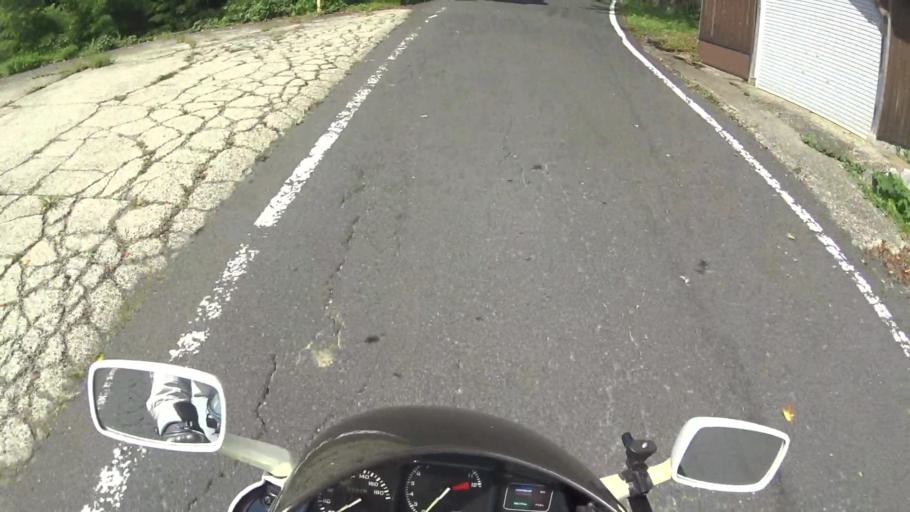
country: JP
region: Kyoto
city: Miyazu
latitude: 35.6732
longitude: 135.2441
